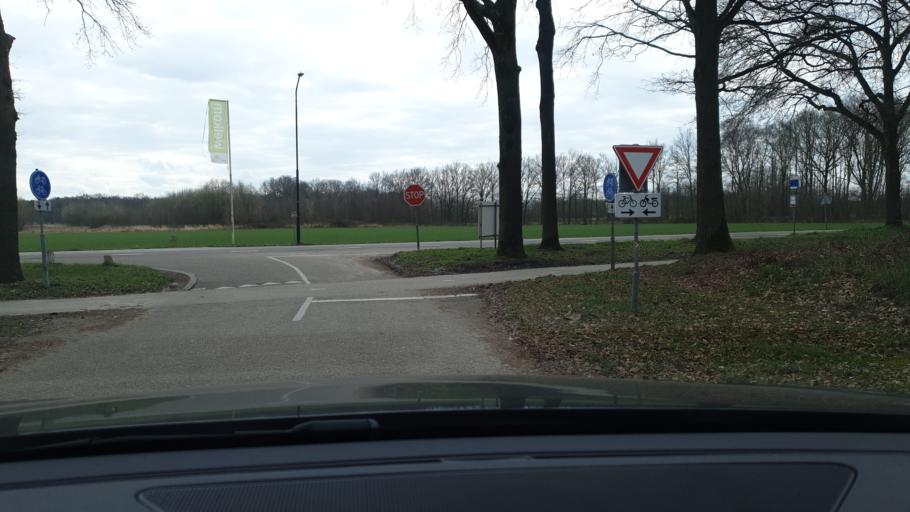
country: NL
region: North Brabant
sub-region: Gemeente Oirschot
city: Oostelbeers
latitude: 51.4109
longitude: 5.2760
